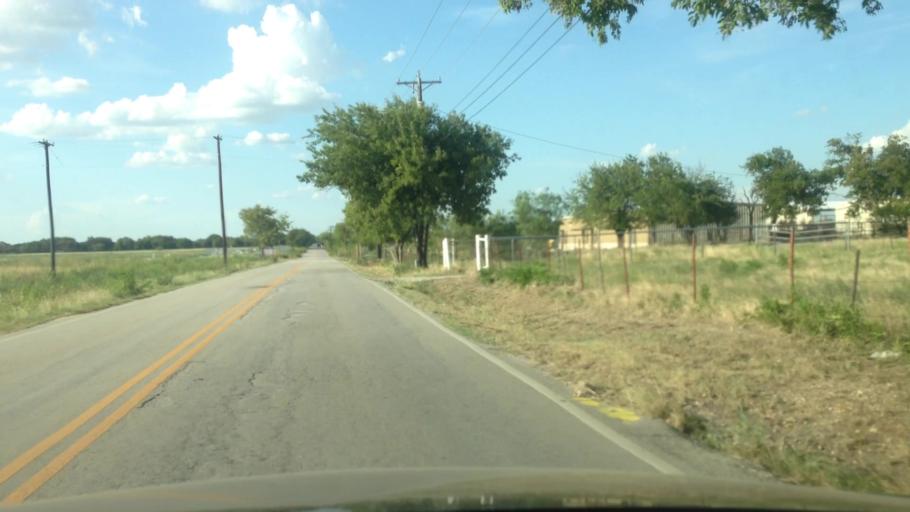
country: US
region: Texas
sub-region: Tarrant County
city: Haslet
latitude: 32.9525
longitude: -97.3919
